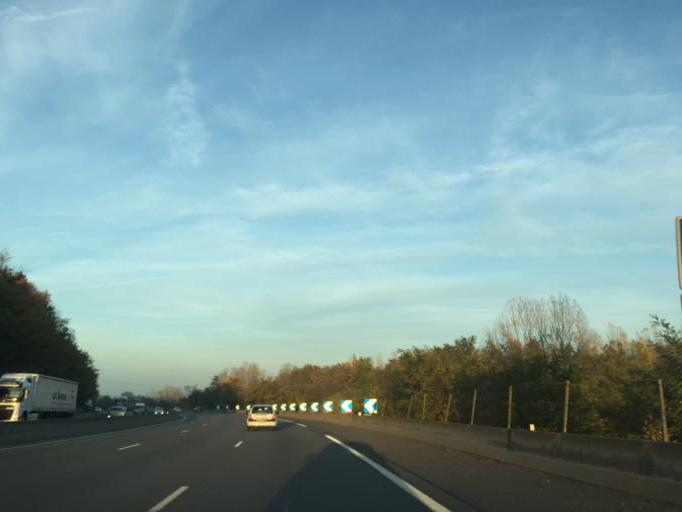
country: FR
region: Rhone-Alpes
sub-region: Departement de la Loire
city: Saint-Jean-Bonnefonds
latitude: 45.4419
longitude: 4.4623
